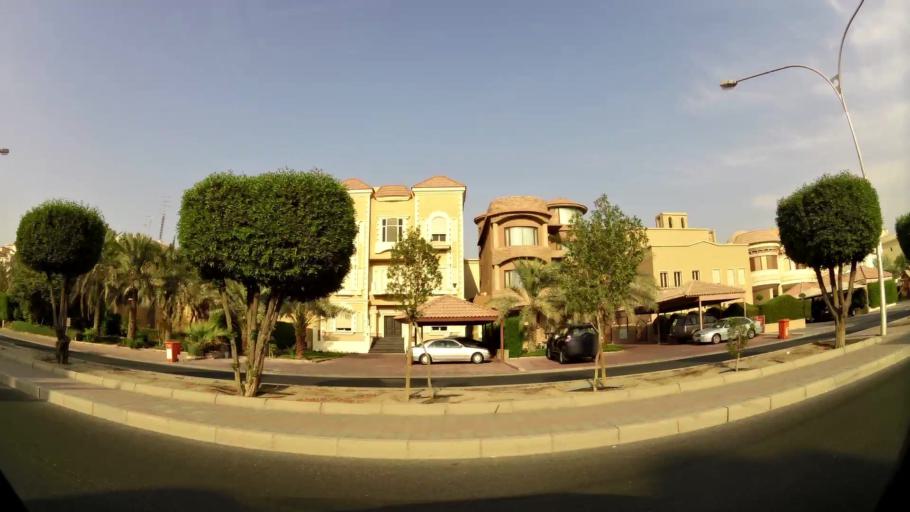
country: KW
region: Muhafazat Hawalli
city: Hawalli
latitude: 29.3164
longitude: 48.0089
